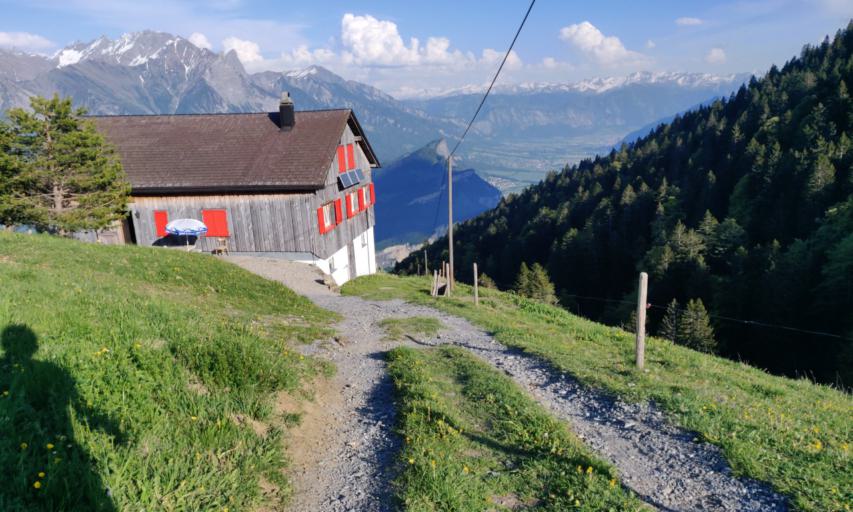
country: CH
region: Saint Gallen
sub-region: Wahlkreis Sarganserland
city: Sargans
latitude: 47.0764
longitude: 9.4385
